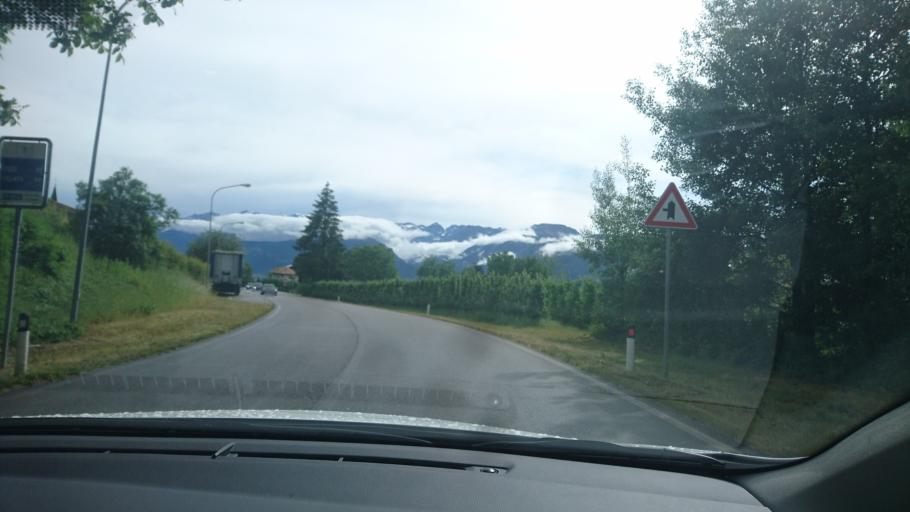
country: IT
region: Trentino-Alto Adige
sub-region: Provincia di Trento
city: Sanzeno
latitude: 46.3811
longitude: 11.0903
